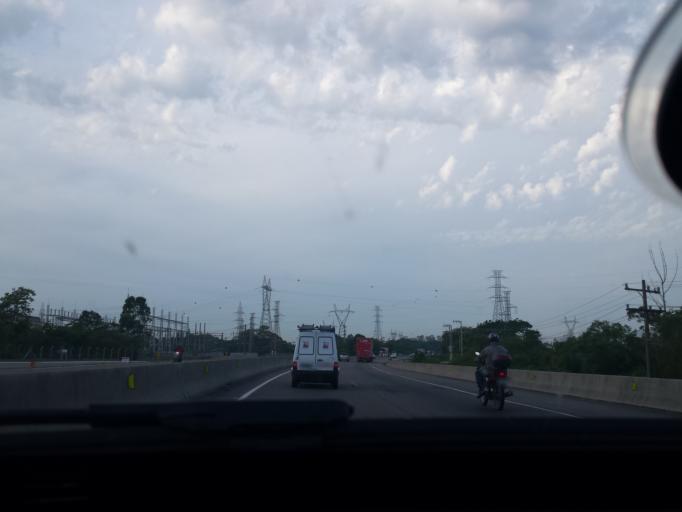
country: BR
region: Santa Catarina
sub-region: Tubarao
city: Tubarao
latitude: -28.4478
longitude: -48.9692
